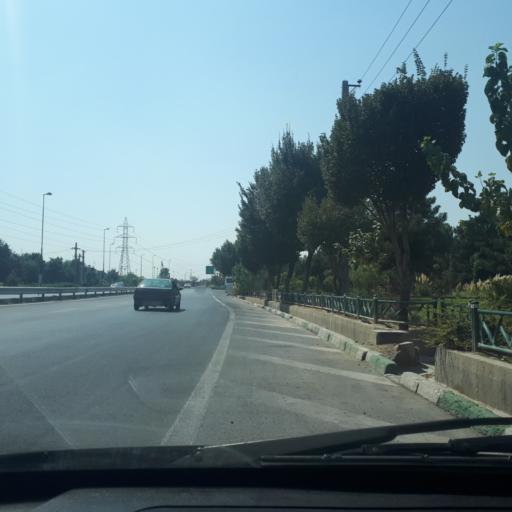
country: IR
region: Tehran
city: Tehran
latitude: 35.7043
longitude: 51.5077
